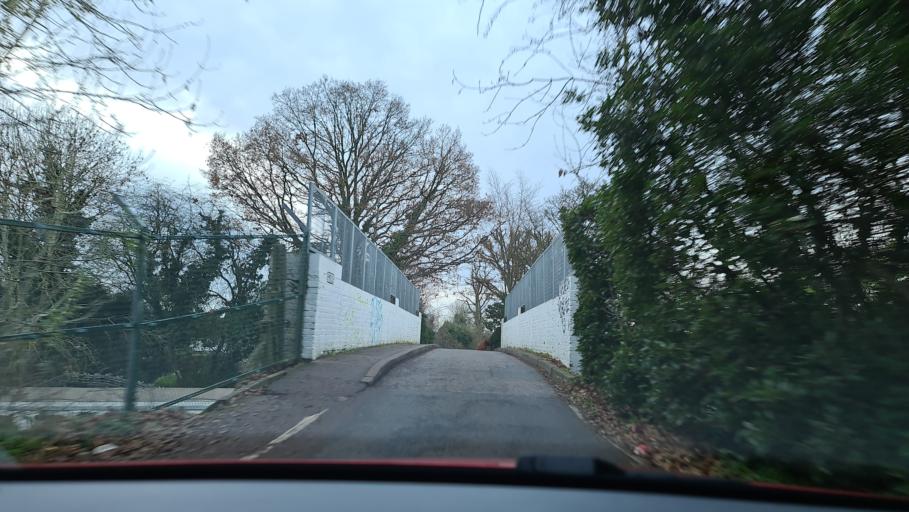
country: GB
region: England
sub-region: Buckinghamshire
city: Amersham on the Hill
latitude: 51.6736
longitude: -0.6012
